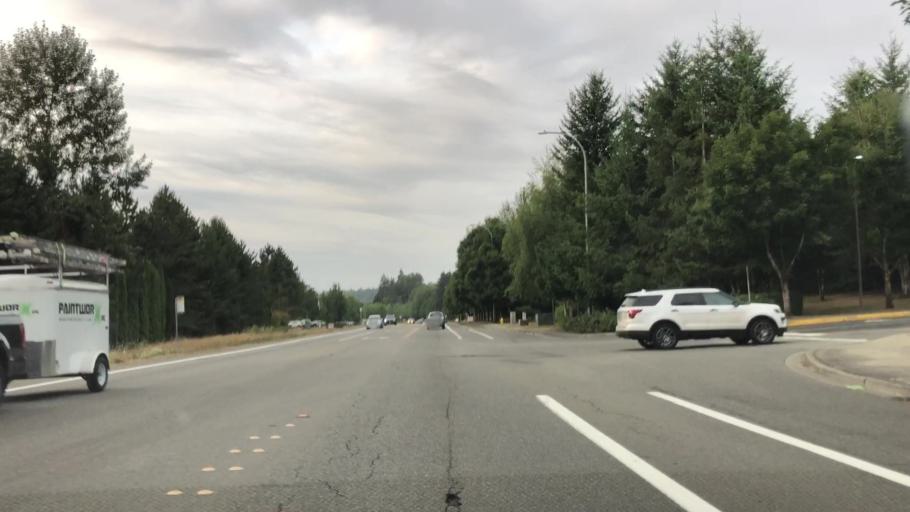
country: US
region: Washington
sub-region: King County
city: Redmond
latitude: 47.6956
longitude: -122.1516
